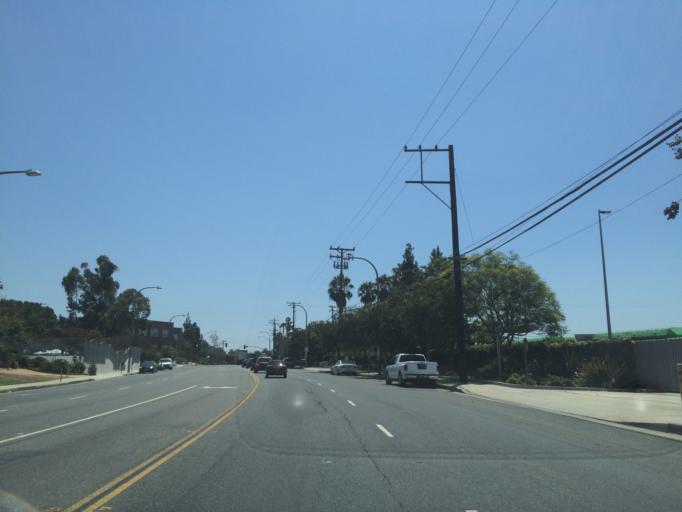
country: US
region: California
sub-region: Los Angeles County
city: Culver City
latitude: 34.0164
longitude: -118.3882
